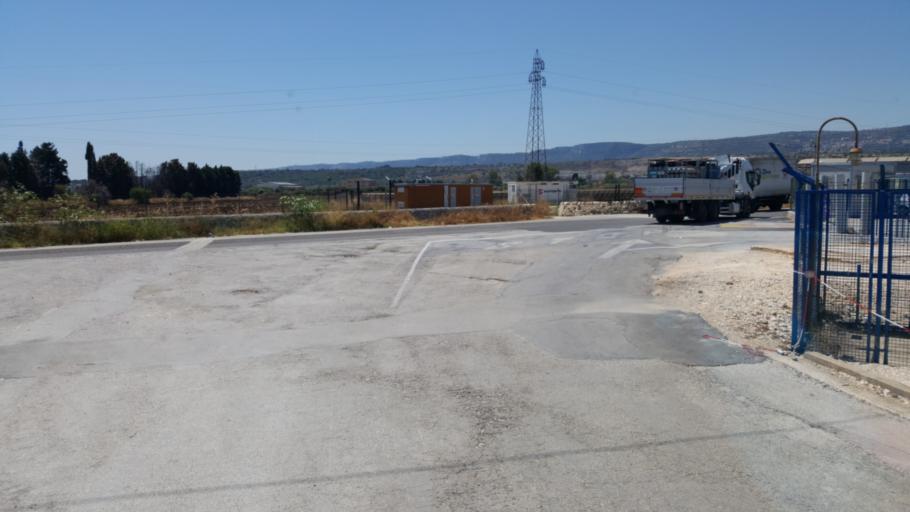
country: IT
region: Sicily
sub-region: Provincia di Siracusa
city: Melilli
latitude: 37.2058
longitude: 15.1666
